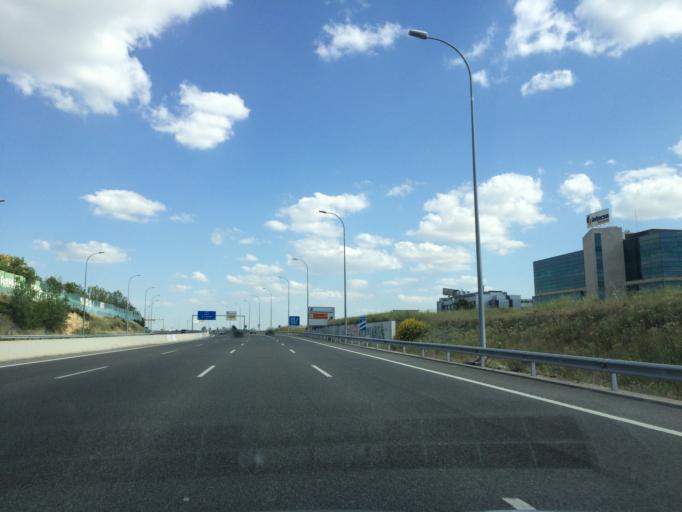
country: ES
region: Madrid
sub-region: Provincia de Madrid
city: Hortaleza
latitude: 40.4766
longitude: -3.6320
